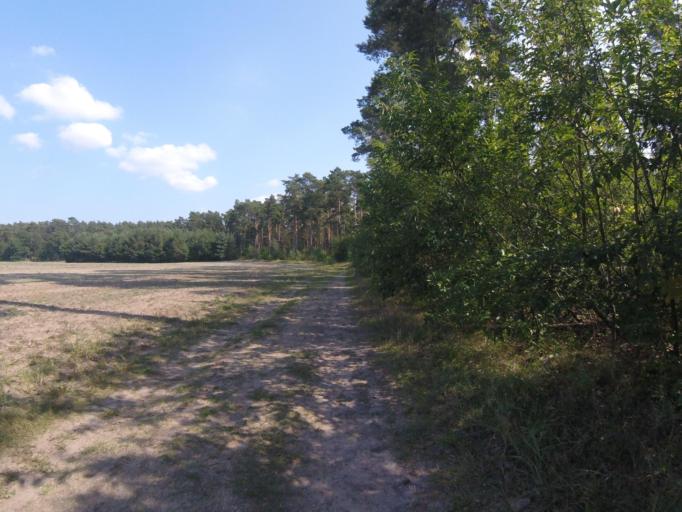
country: DE
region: Brandenburg
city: Bestensee
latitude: 52.2606
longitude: 13.7580
